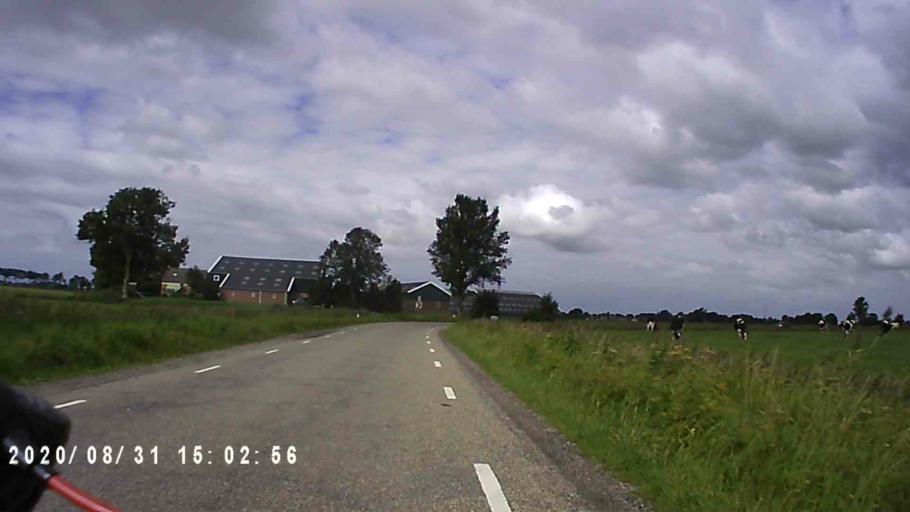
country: NL
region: Groningen
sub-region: Gemeente Zuidhorn
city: Oldehove
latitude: 53.2920
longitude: 6.3926
